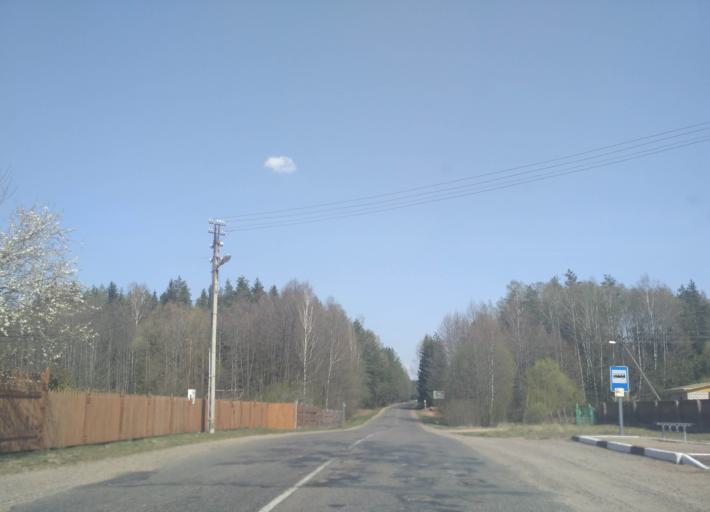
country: BY
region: Minsk
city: Loshnitsa
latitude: 54.4219
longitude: 28.6475
